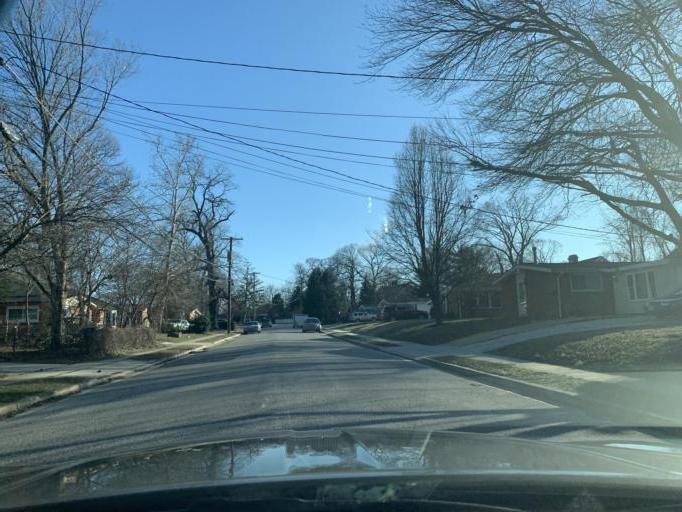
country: US
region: Maryland
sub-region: Anne Arundel County
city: Glen Burnie
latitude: 39.1477
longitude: -76.6300
